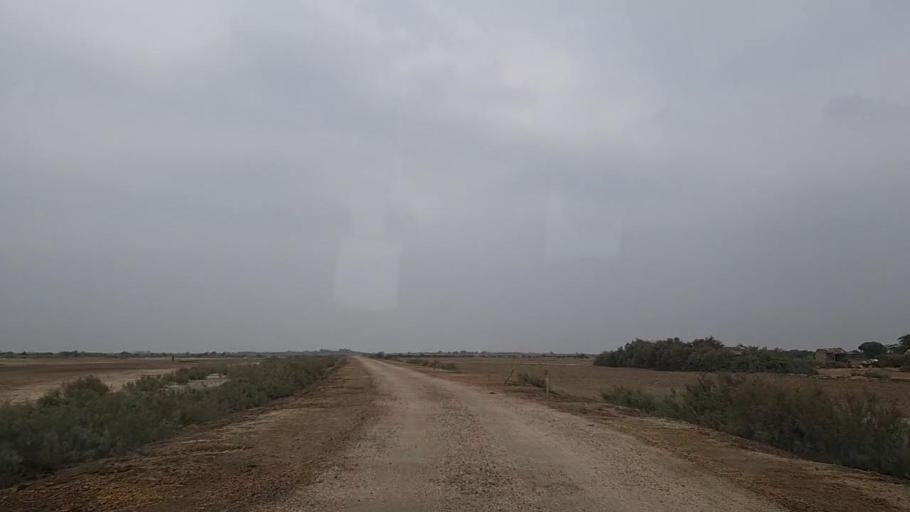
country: PK
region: Sindh
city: Mirpur Sakro
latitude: 24.6258
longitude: 67.7188
